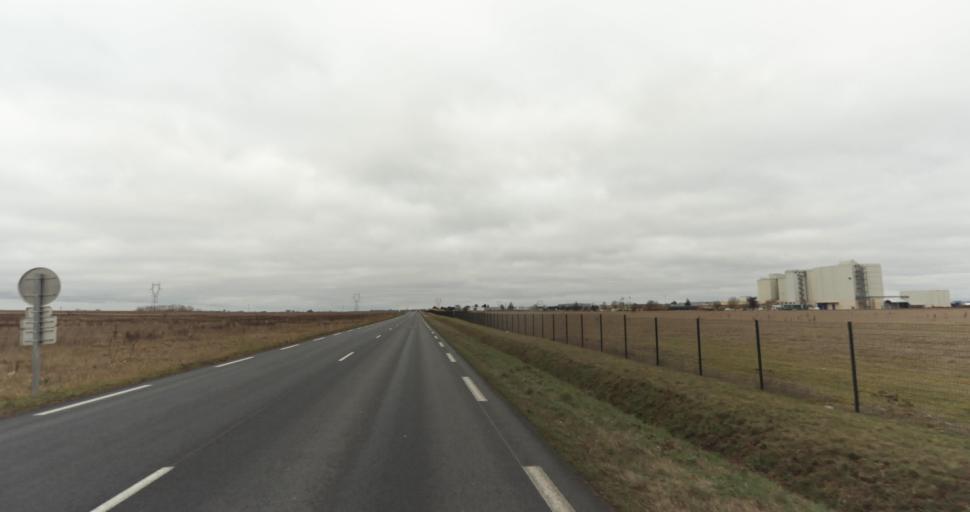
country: FR
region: Pays de la Loire
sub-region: Departement de Maine-et-Loire
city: Montreuil-Bellay
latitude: 47.1033
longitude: -0.1013
